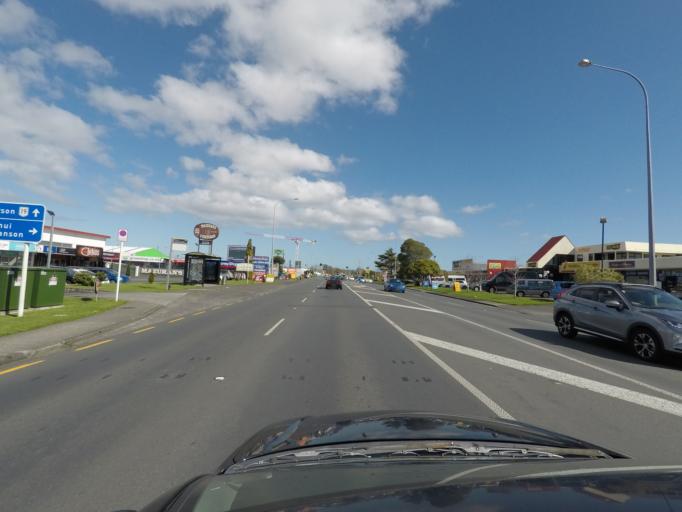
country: NZ
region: Auckland
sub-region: Auckland
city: Rosebank
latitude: -36.8552
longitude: 174.6300
